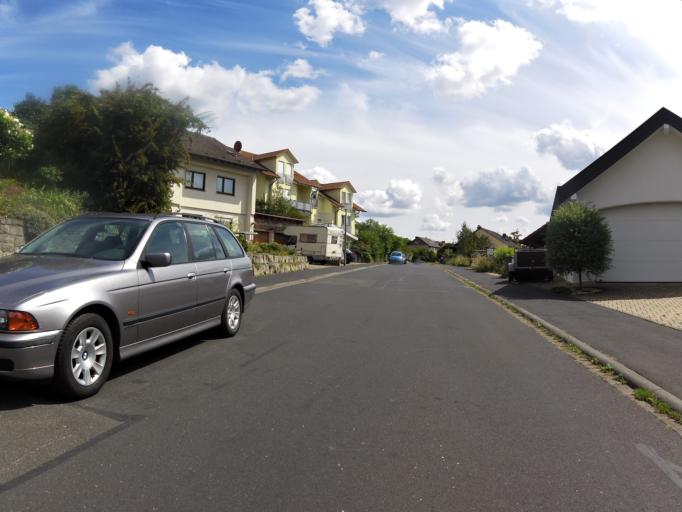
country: DE
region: Bavaria
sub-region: Regierungsbezirk Unterfranken
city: Sommerhausen
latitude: 49.7055
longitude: 10.0277
